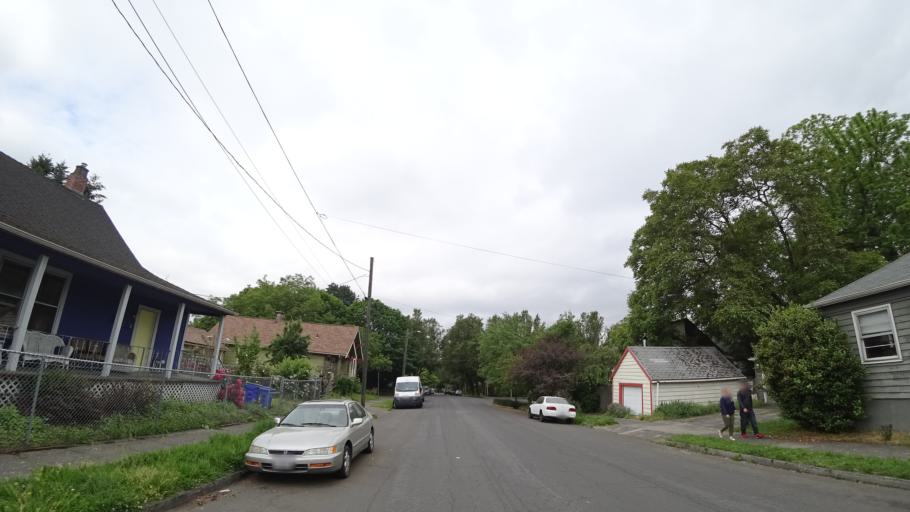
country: US
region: Oregon
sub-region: Multnomah County
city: Portland
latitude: 45.5005
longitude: -122.6399
